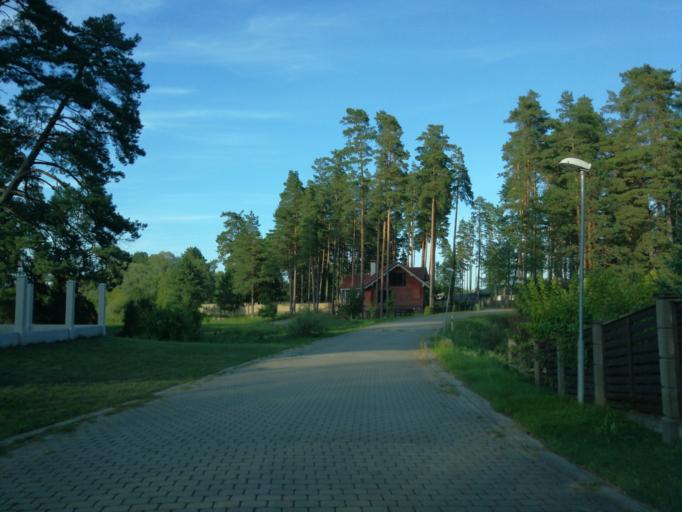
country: LV
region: Garkalne
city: Garkalne
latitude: 57.0851
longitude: 24.4726
